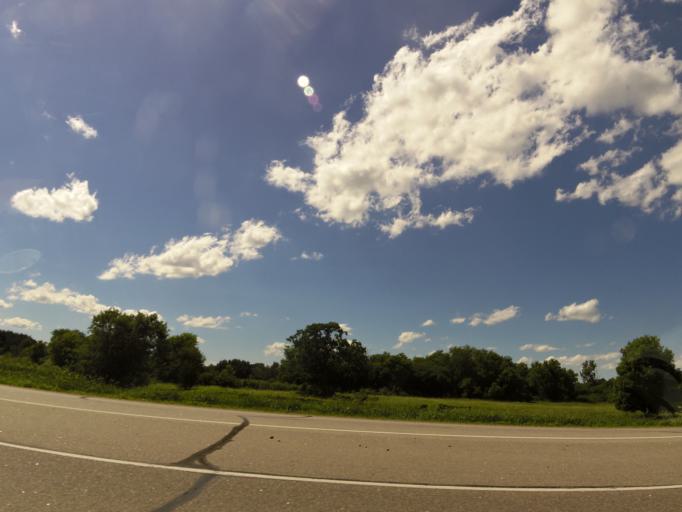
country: US
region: Minnesota
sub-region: Stearns County
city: Saint Augusta
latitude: 45.4935
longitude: -94.2445
